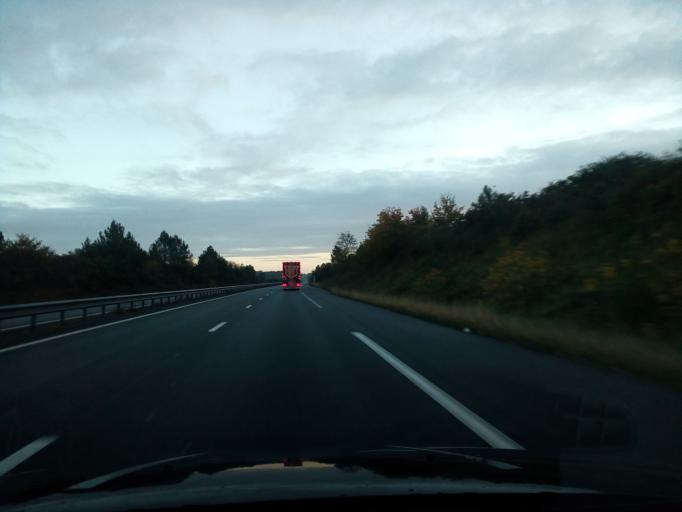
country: FR
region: Poitou-Charentes
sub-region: Departement de la Charente-Maritime
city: Montlieu-la-Garde
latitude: 45.2057
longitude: -0.2998
